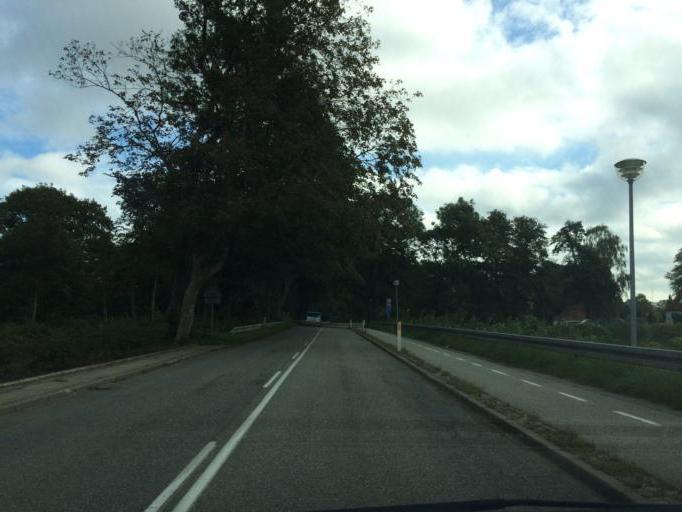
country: DK
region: North Denmark
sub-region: Bronderslev Kommune
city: Dronninglund
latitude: 57.1564
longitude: 10.2599
